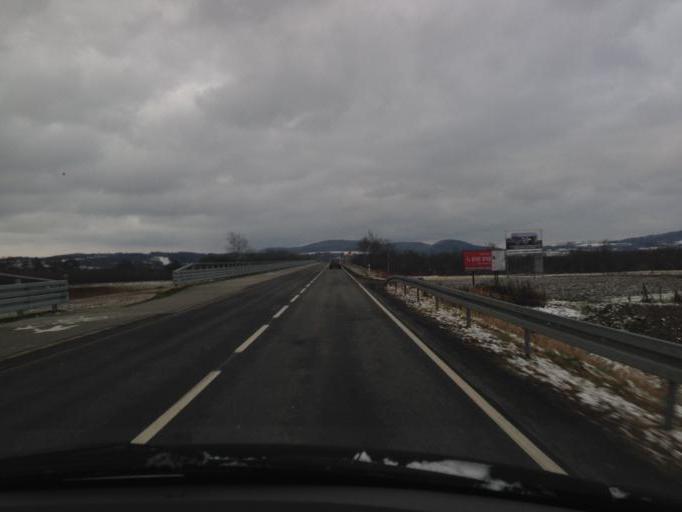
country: PL
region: Lesser Poland Voivodeship
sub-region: Powiat tarnowski
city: Zakliczyn
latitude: 49.8693
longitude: 20.8113
